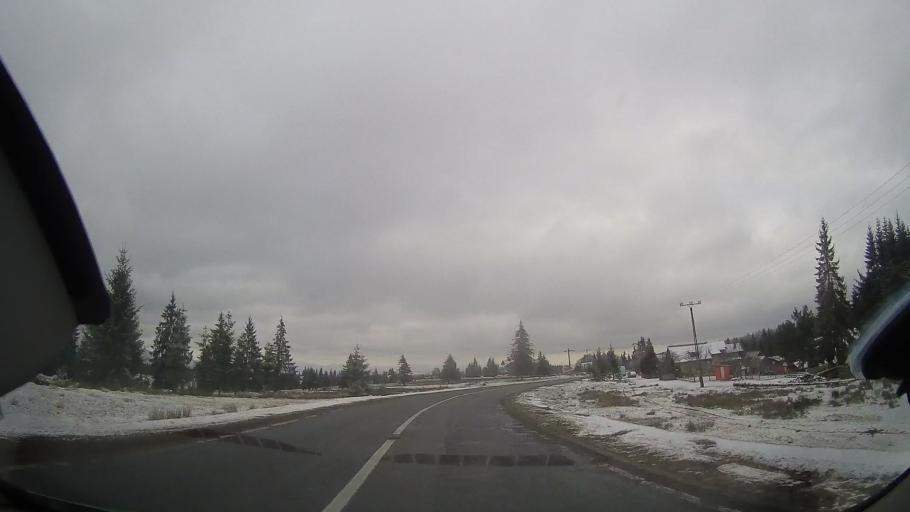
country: RO
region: Cluj
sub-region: Comuna Belis
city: Belis
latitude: 46.7011
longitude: 23.0362
